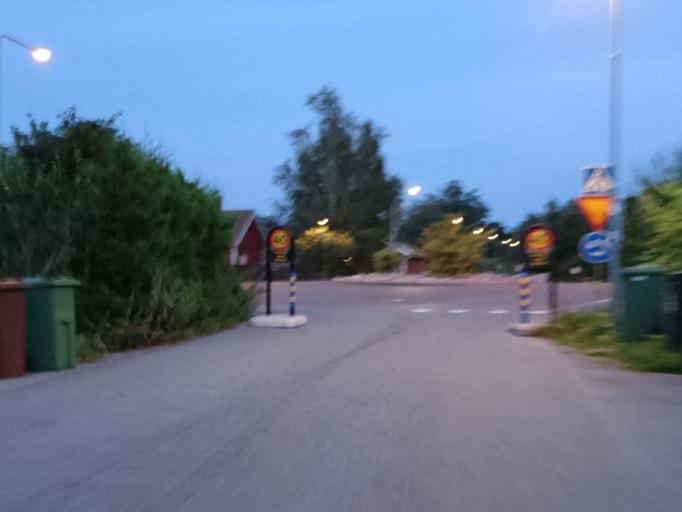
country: SE
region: Stockholm
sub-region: Huddinge Kommun
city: Segeltorp
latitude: 59.2791
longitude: 17.9389
